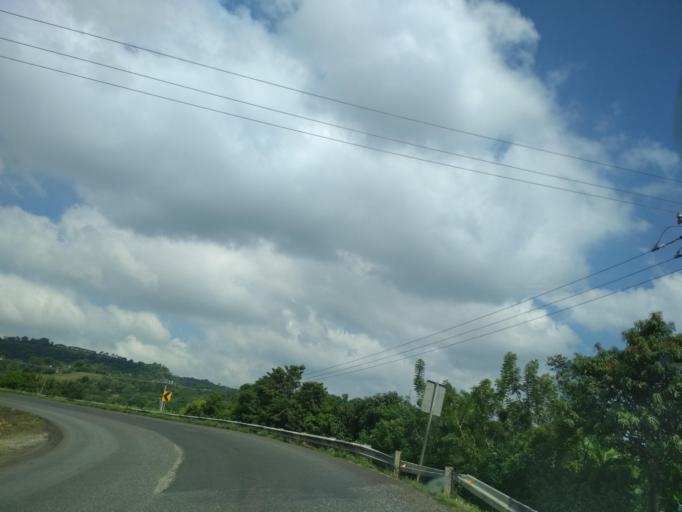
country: MX
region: Veracruz
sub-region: San Andres Tuxtla
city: Texcaltitan Xoteapan (Texcaltitan)
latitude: 18.4396
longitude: -95.2625
